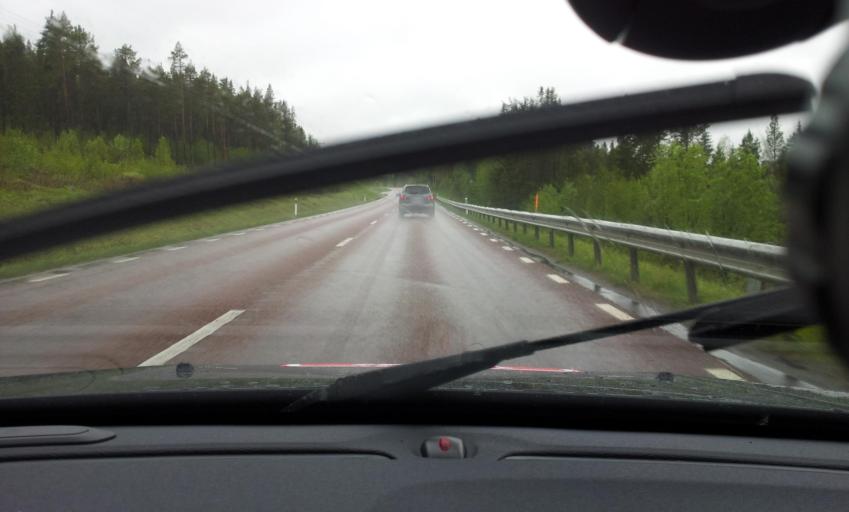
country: SE
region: Jaemtland
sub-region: Bergs Kommun
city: Hoverberg
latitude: 62.7803
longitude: 14.4527
